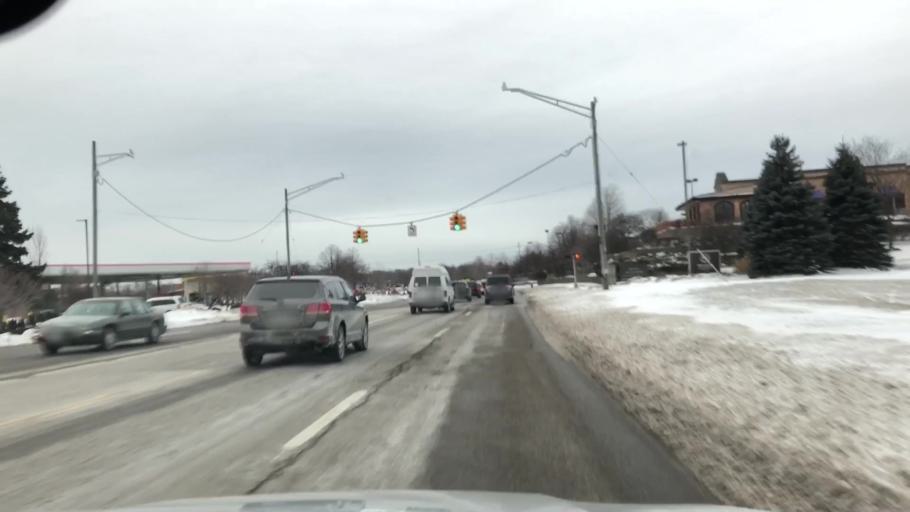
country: US
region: Michigan
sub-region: Wayne County
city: Northville
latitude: 42.4422
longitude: -83.4349
